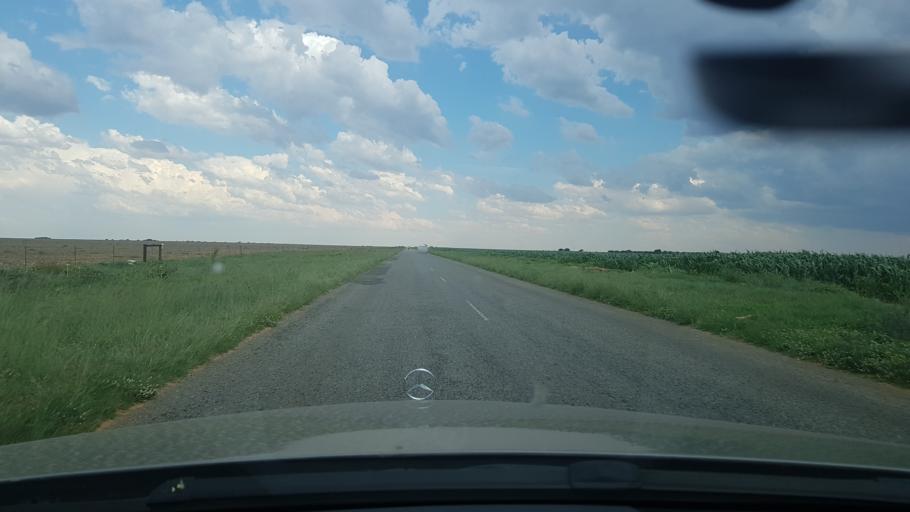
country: ZA
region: Orange Free State
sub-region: Lejweleputswa District Municipality
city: Hoopstad
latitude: -27.8962
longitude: 25.6724
